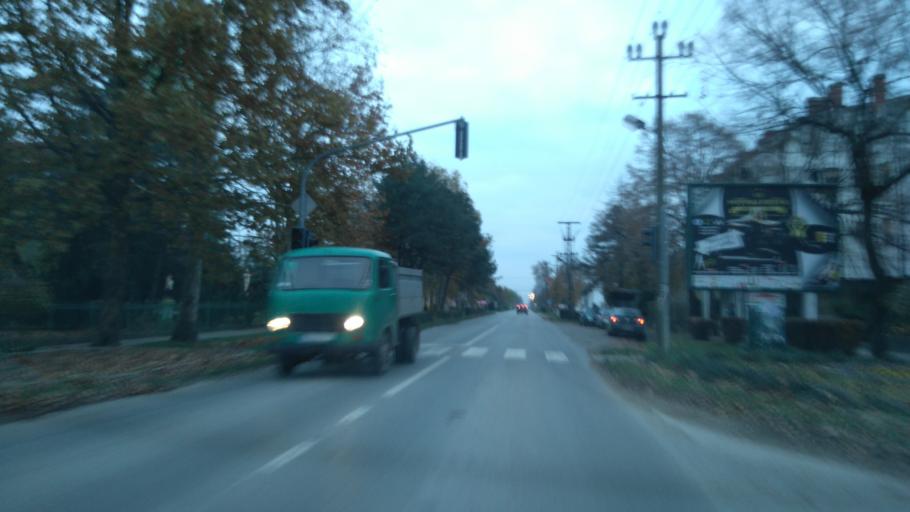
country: RS
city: Mol
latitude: 45.7639
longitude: 20.1296
